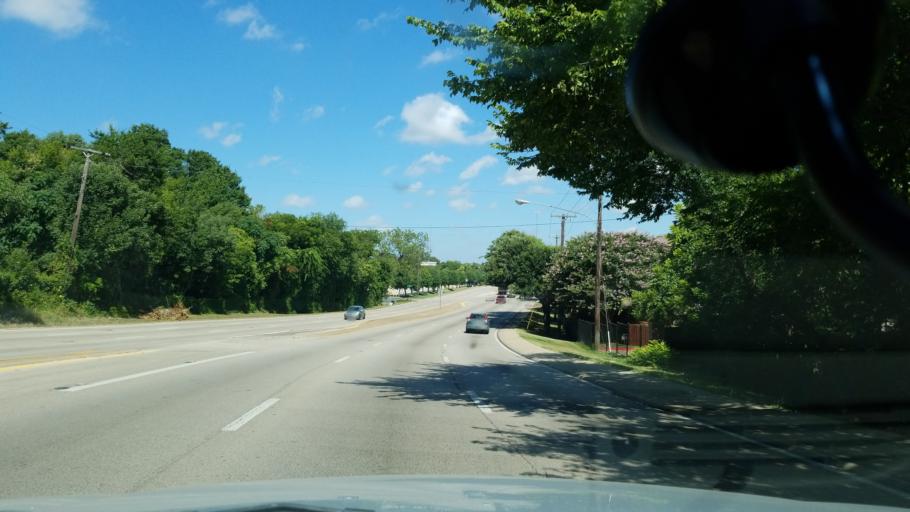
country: US
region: Texas
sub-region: Dallas County
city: Cockrell Hill
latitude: 32.6841
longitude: -96.8173
